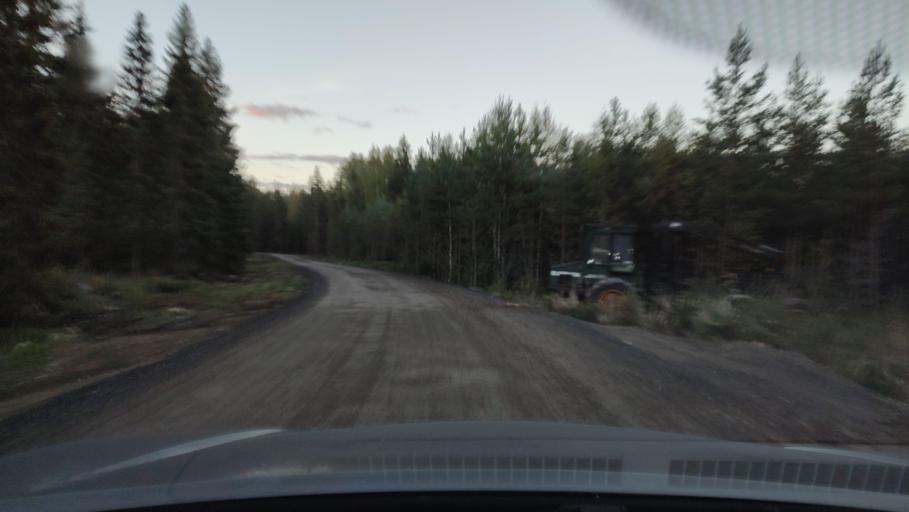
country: FI
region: Southern Ostrobothnia
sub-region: Suupohja
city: Karijoki
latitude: 62.1862
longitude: 21.5882
